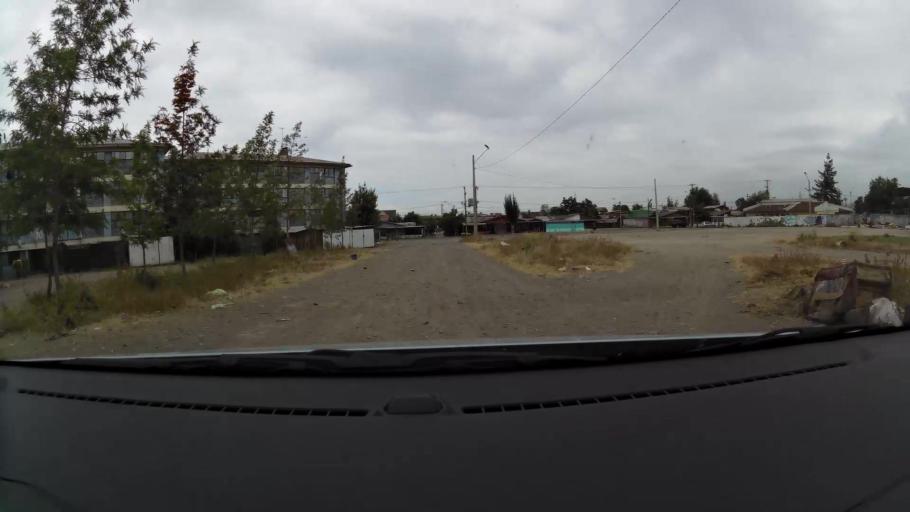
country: CL
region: Santiago Metropolitan
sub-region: Provincia de Maipo
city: San Bernardo
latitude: -33.5241
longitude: -70.6891
